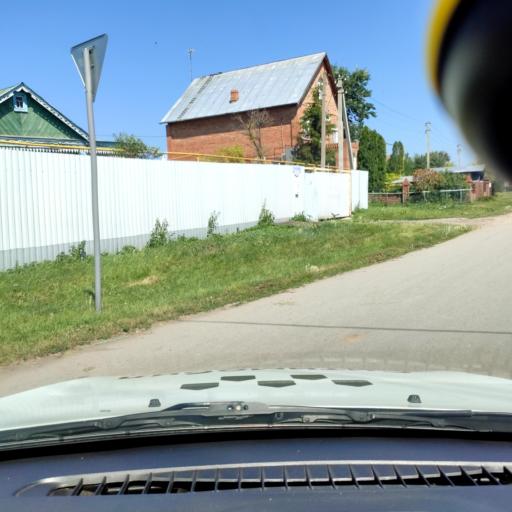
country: RU
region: Samara
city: Tol'yatti
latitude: 53.6385
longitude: 49.2911
